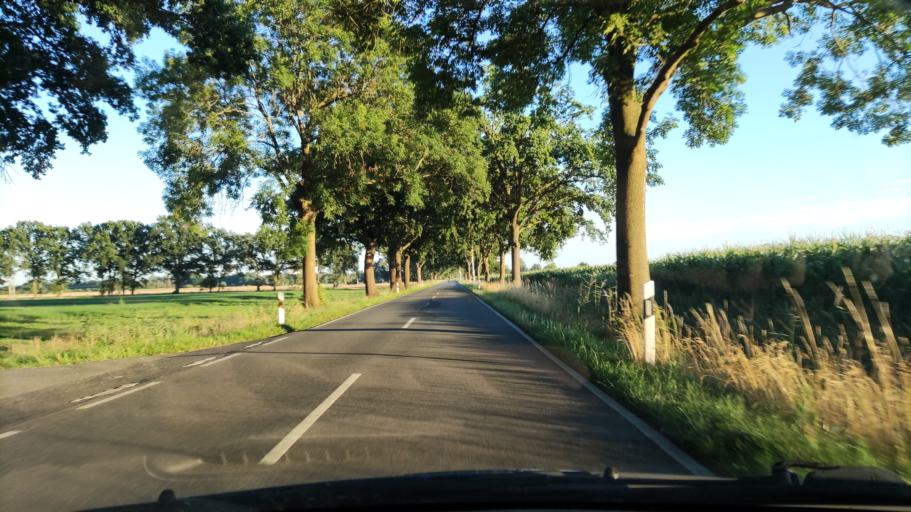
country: DE
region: Lower Saxony
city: Luechow
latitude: 52.9955
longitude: 11.1535
